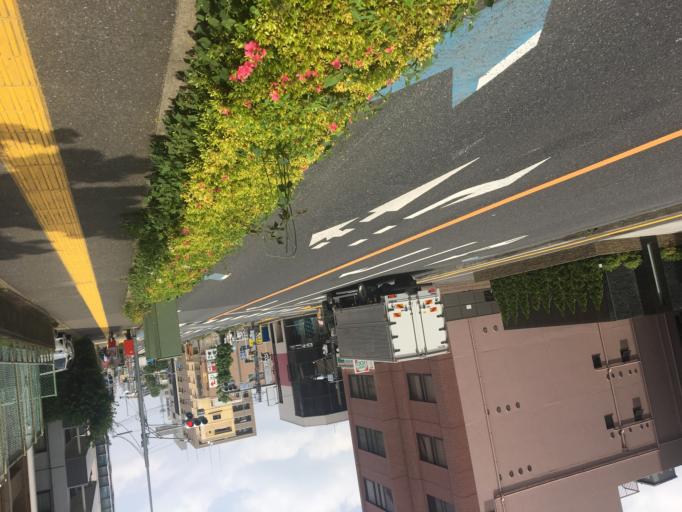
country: JP
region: Saitama
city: Yono
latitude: 35.8584
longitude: 139.6472
